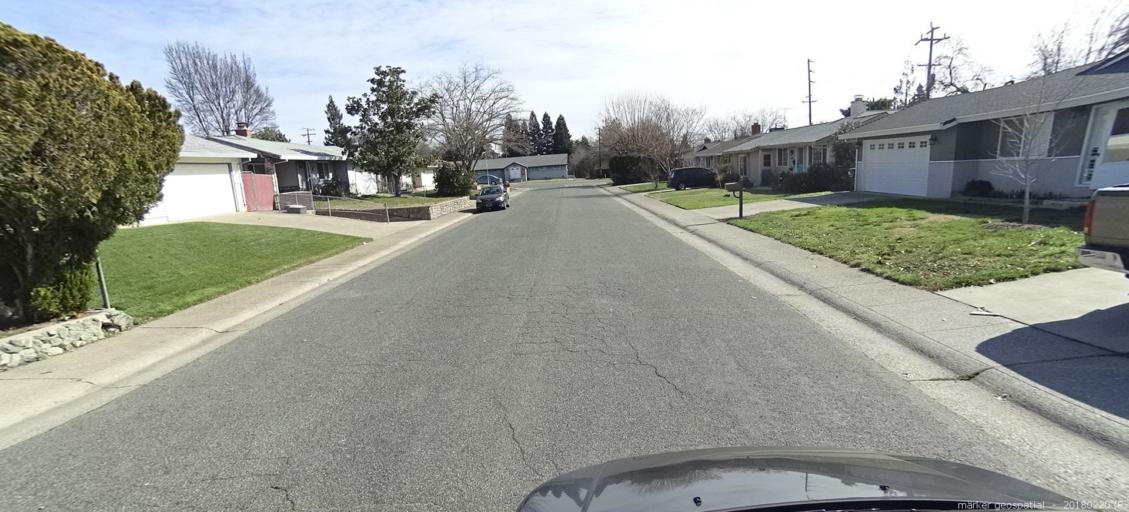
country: US
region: California
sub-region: Sacramento County
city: Orangevale
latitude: 38.6732
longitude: -121.2176
